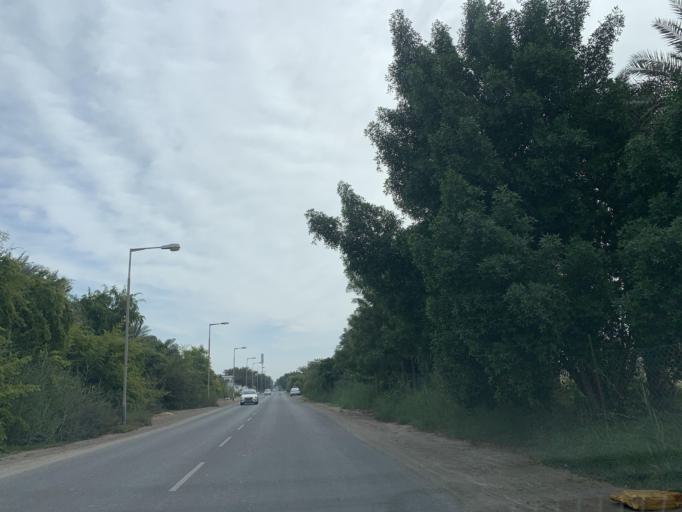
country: BH
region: Central Governorate
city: Madinat Hamad
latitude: 26.1275
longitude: 50.4705
